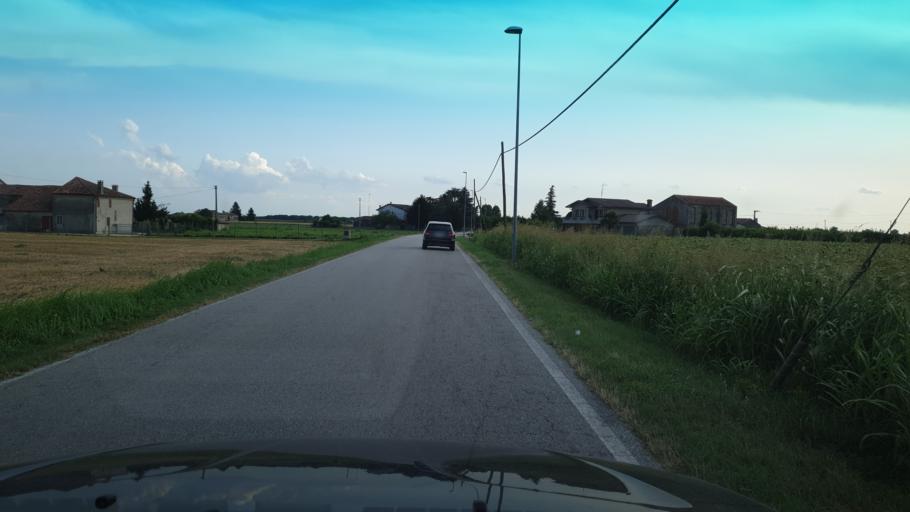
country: IT
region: Veneto
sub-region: Provincia di Rovigo
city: Castelguglielmo
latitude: 45.0166
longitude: 11.5328
